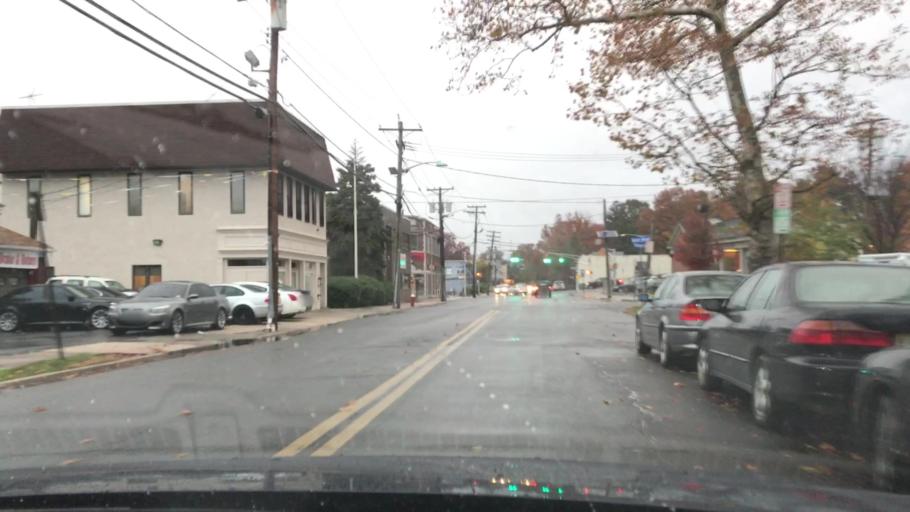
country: US
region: New Jersey
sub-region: Bergen County
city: Teaneck
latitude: 40.8869
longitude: -74.0195
